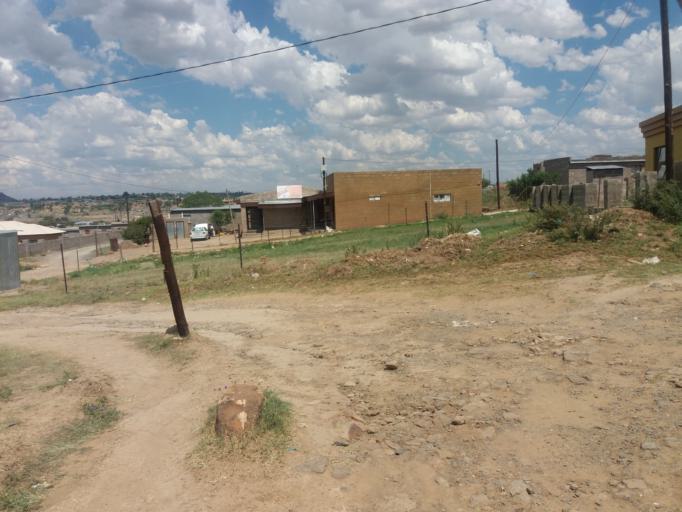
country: LS
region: Maseru
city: Maseru
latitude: -29.3654
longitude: 27.4755
